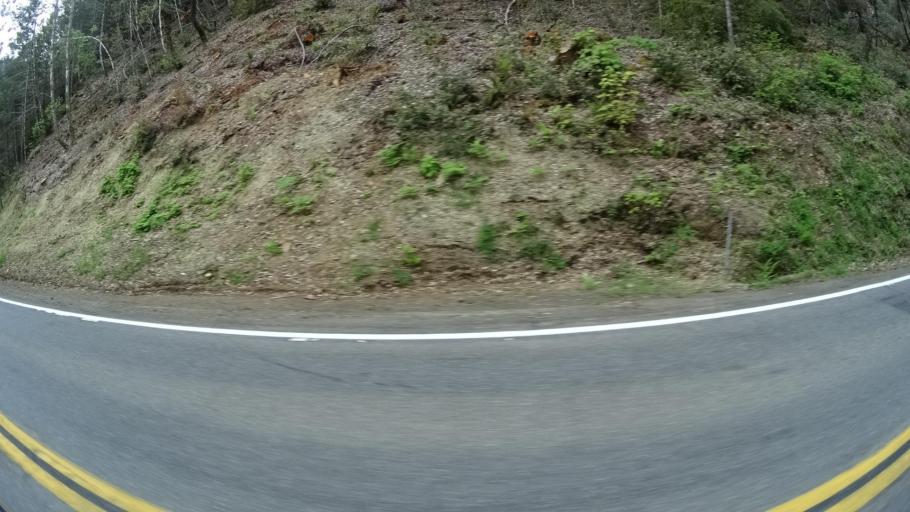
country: US
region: California
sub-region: Humboldt County
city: Willow Creek
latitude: 41.0003
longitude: -123.6265
